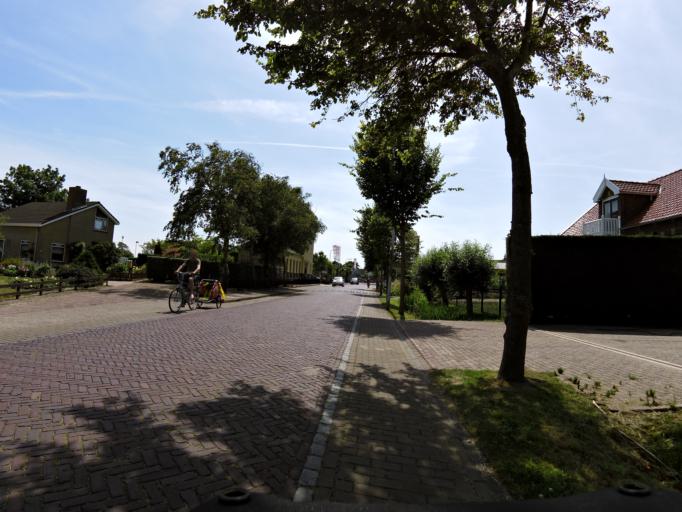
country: NL
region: Zeeland
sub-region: Schouwen-Duiveland
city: Burgh
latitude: 51.6934
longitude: 3.7363
